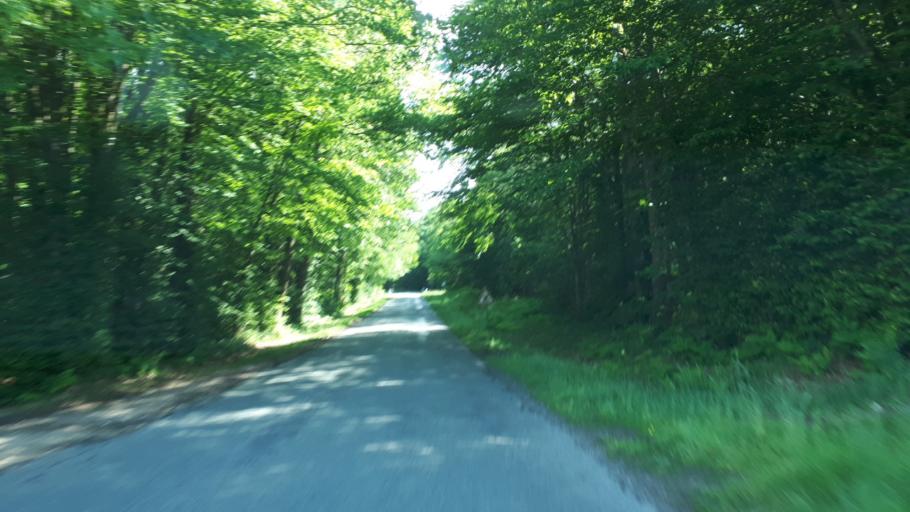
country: FR
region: Centre
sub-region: Departement du Cher
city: Henrichemont
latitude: 47.3972
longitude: 2.5943
